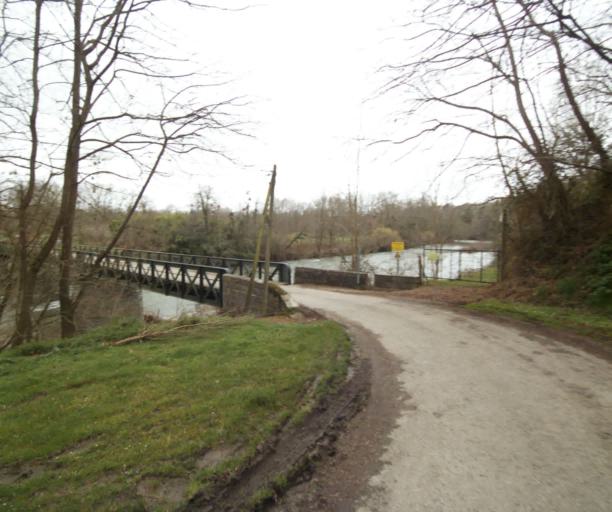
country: FR
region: Midi-Pyrenees
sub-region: Departement de l'Ariege
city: Saverdun
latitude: 43.1837
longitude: 1.5987
